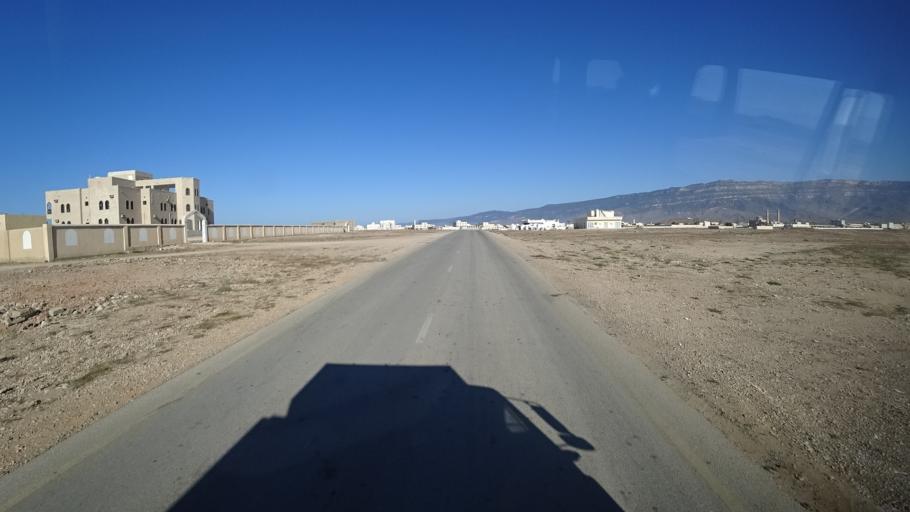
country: OM
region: Zufar
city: Salalah
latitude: 16.9796
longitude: 54.6983
